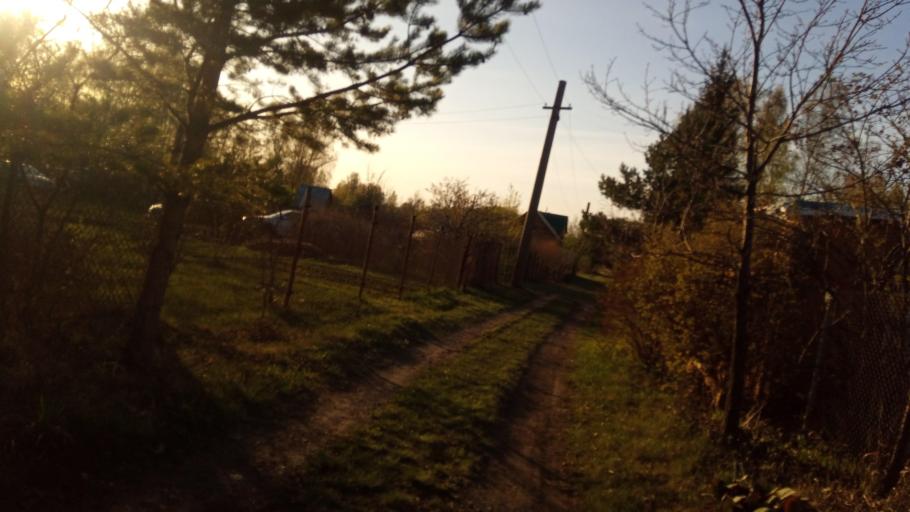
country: RU
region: Chelyabinsk
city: Timiryazevskiy
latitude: 54.9935
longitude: 60.8491
